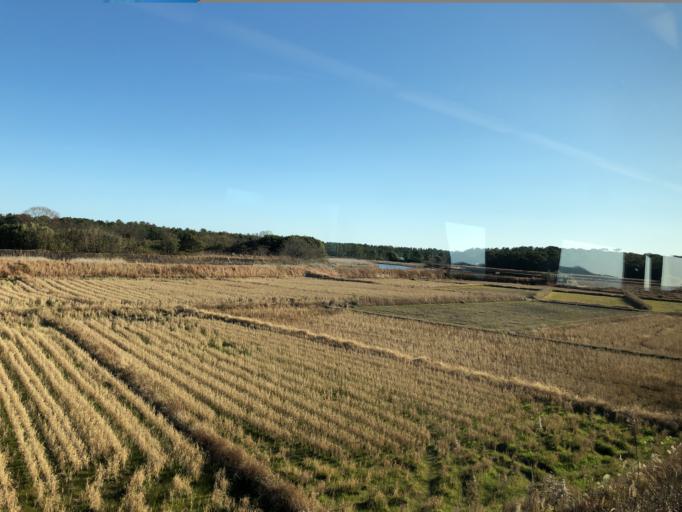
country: JP
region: Kochi
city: Nakamura
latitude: 33.0342
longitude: 133.0189
